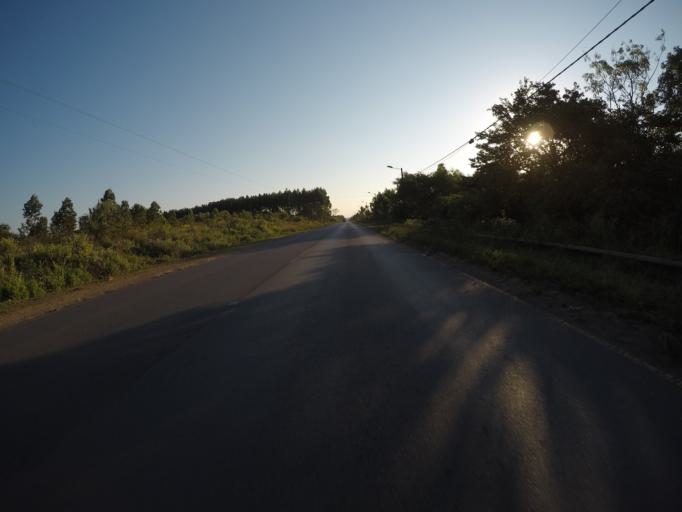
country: ZA
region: KwaZulu-Natal
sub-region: uThungulu District Municipality
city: KwaMbonambi
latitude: -28.6830
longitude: 32.1947
